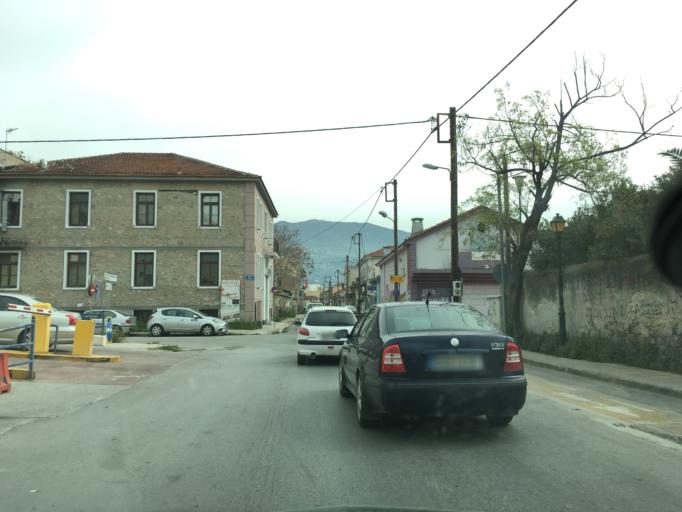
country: GR
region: Thessaly
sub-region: Nomos Magnisias
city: Nea Ionia
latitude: 39.3611
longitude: 22.9340
